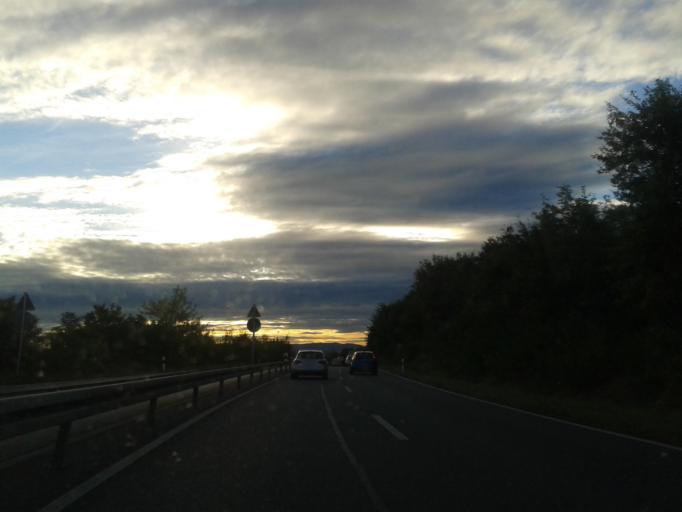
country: DE
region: Saxony
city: Radebeul
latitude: 51.0733
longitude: 13.6572
